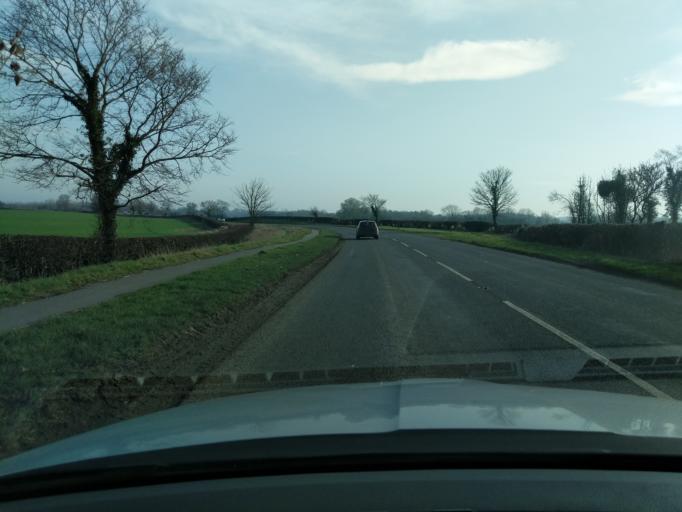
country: GB
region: England
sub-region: North Yorkshire
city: Bedale
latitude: 54.3011
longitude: -1.6242
